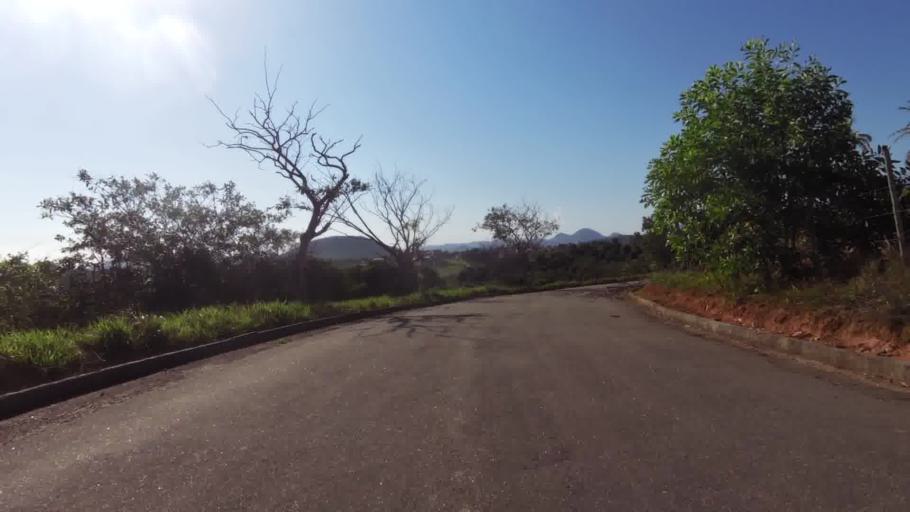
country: BR
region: Espirito Santo
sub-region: Guarapari
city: Guarapari
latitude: -20.7392
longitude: -40.5601
